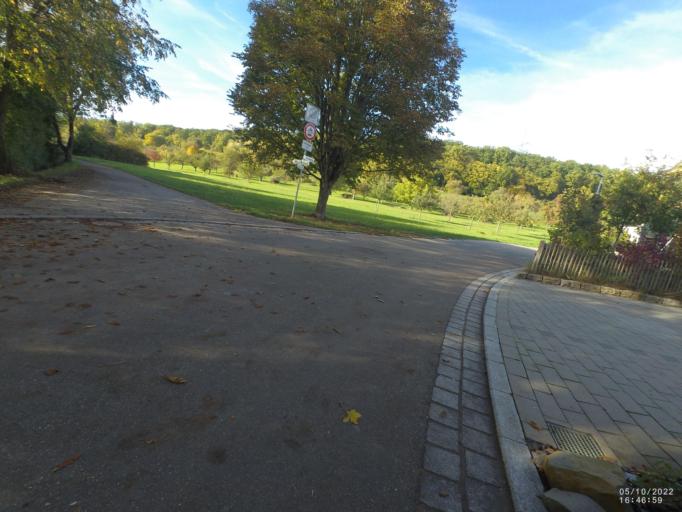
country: DE
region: Baden-Wuerttemberg
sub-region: Regierungsbezirk Stuttgart
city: Schlierbach
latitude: 48.6943
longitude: 9.4986
